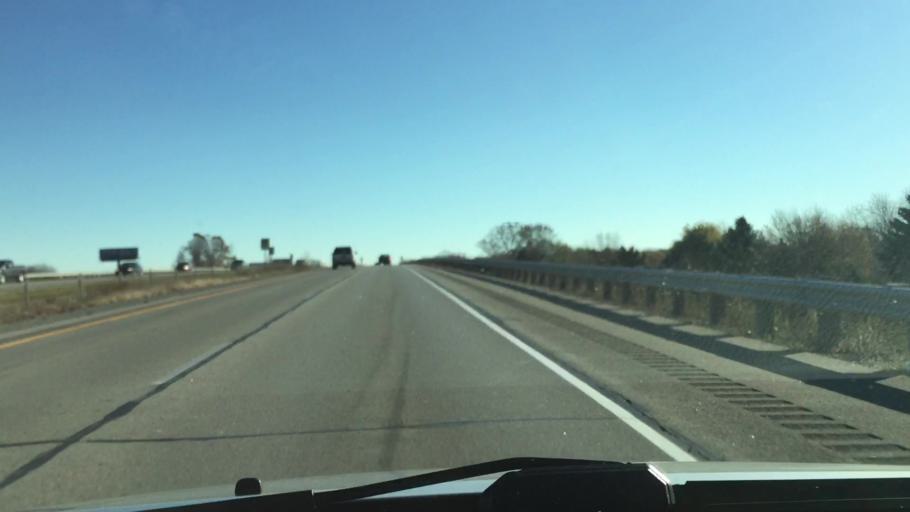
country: US
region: Wisconsin
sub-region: Outagamie County
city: Appleton
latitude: 44.2989
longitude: -88.4392
